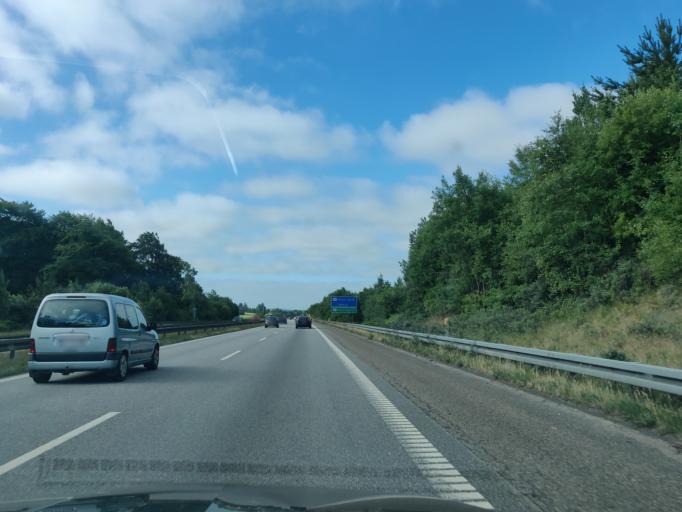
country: DK
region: North Denmark
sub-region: Rebild Kommune
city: Stovring
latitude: 56.9186
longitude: 9.8425
